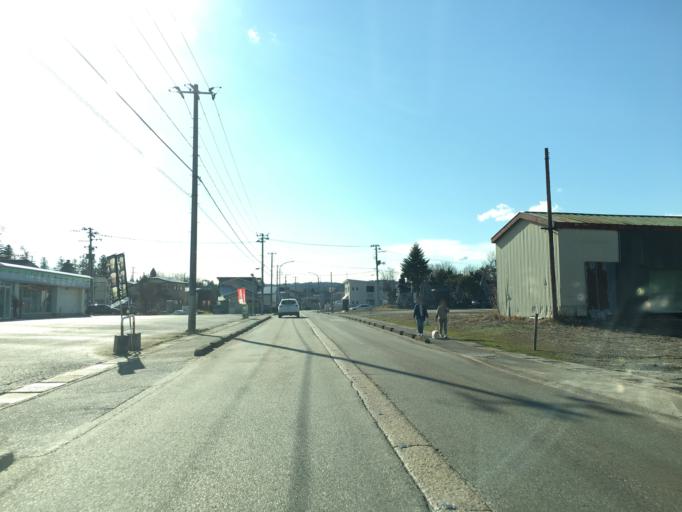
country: JP
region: Yamagata
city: Nagai
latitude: 38.0056
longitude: 140.0392
